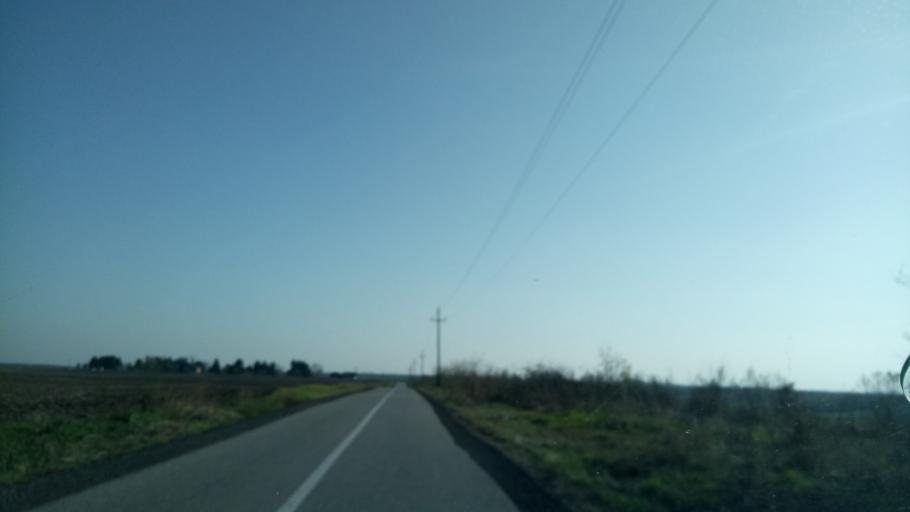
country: RS
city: Ljukovo
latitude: 45.0334
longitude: 20.0446
